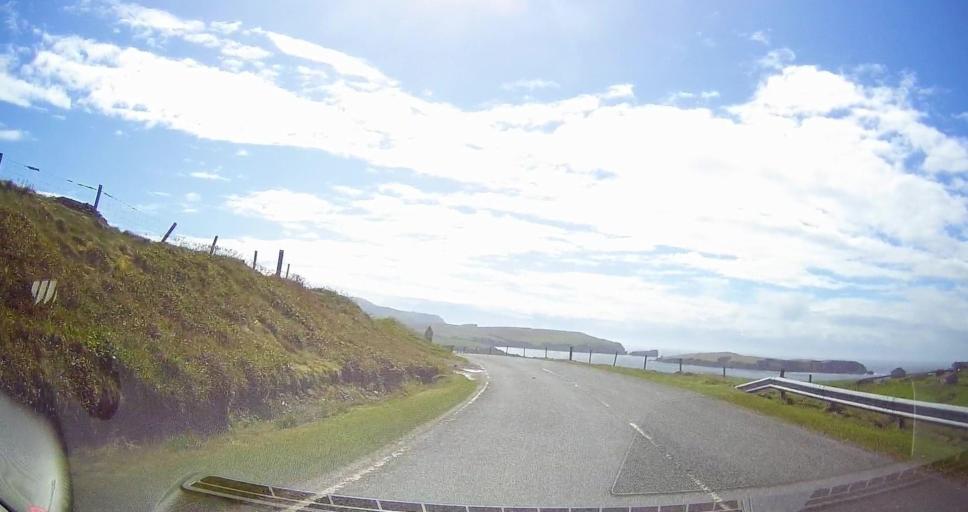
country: GB
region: Scotland
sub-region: Shetland Islands
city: Sandwick
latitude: 59.9587
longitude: -1.3250
